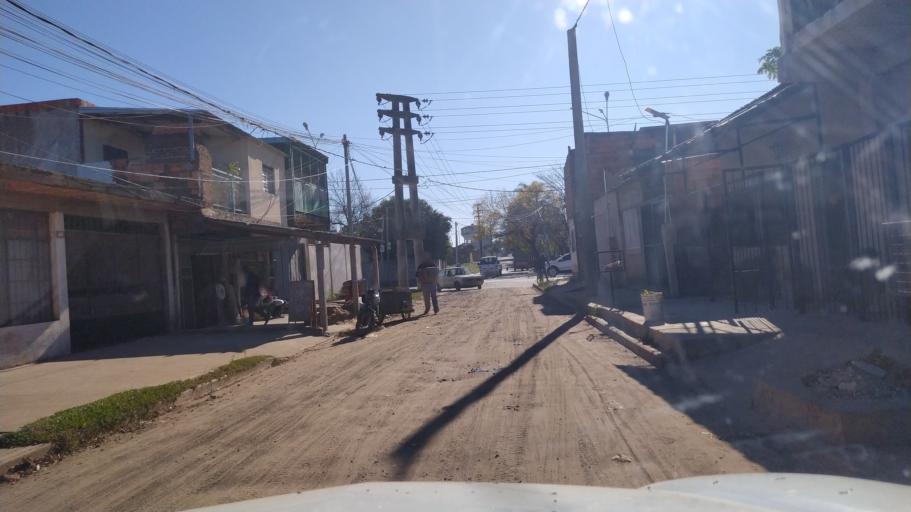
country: AR
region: Corrientes
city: Corrientes
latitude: -27.4943
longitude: -58.8053
